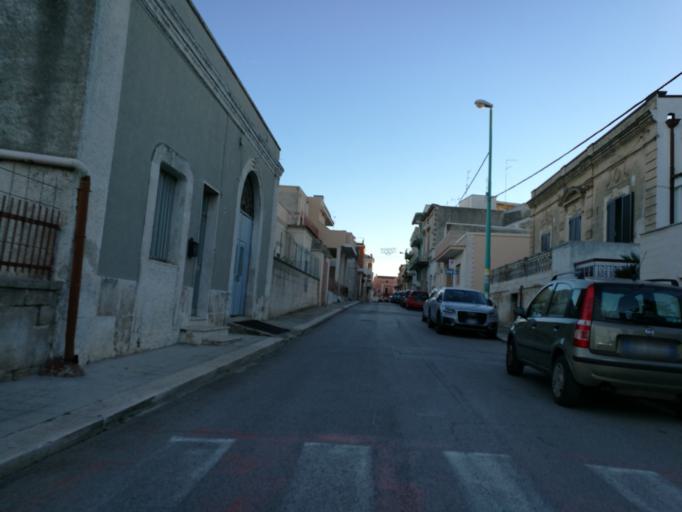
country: IT
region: Apulia
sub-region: Provincia di Bari
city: Adelfia
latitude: 41.0065
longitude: 16.8778
